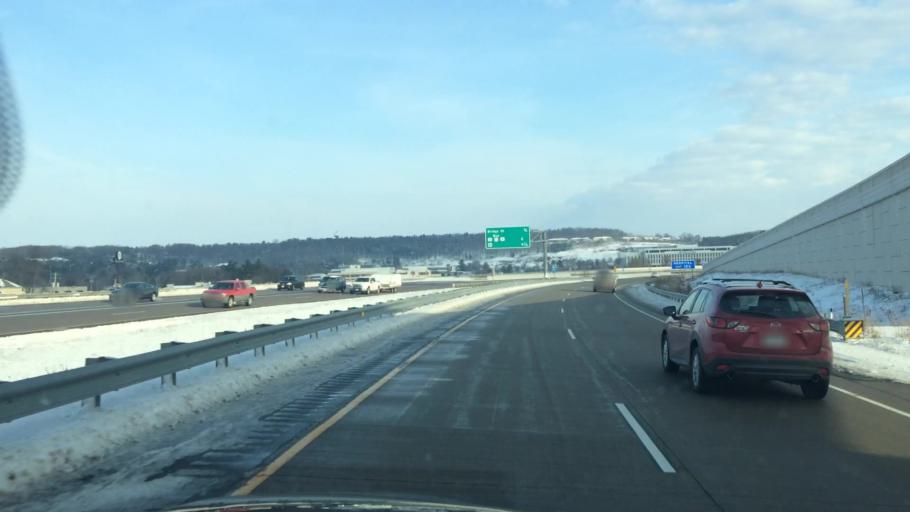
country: US
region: Wisconsin
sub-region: Marathon County
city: Wausau
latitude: 44.9560
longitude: -89.6666
